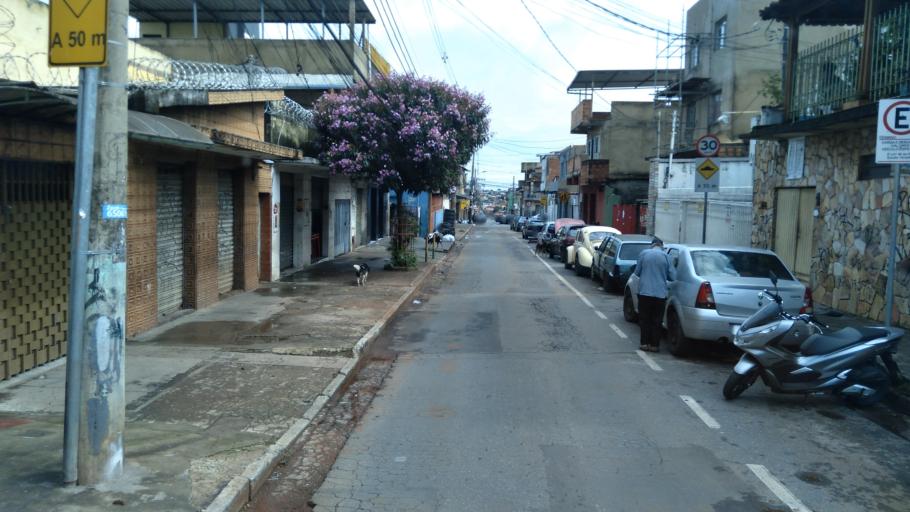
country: BR
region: Minas Gerais
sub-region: Belo Horizonte
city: Belo Horizonte
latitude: -19.9080
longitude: -43.8927
